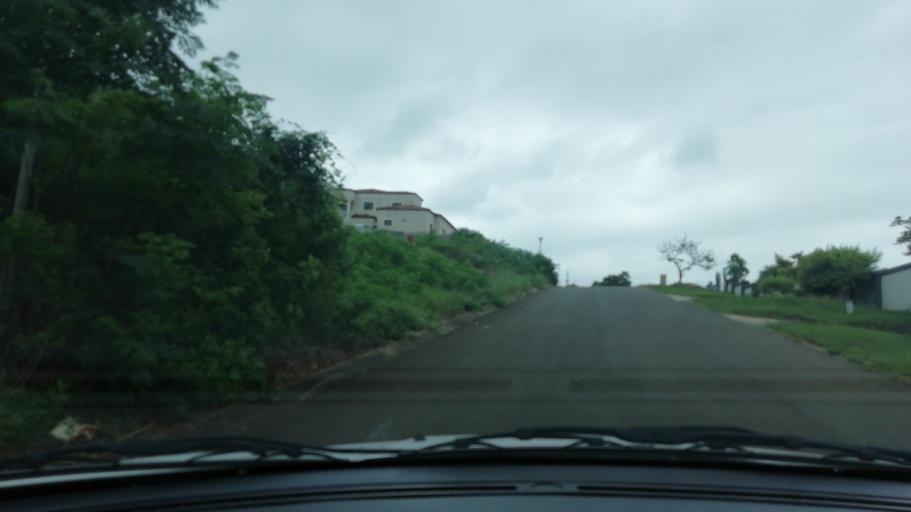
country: ZA
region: KwaZulu-Natal
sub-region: uThungulu District Municipality
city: Empangeni
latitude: -28.7594
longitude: 31.8843
